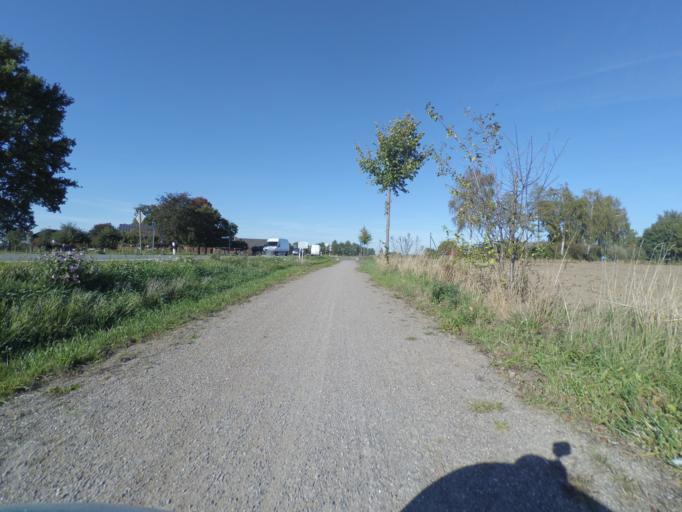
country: DE
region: North Rhine-Westphalia
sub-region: Regierungsbezirk Dusseldorf
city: Bocholt
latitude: 51.8382
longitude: 6.5564
